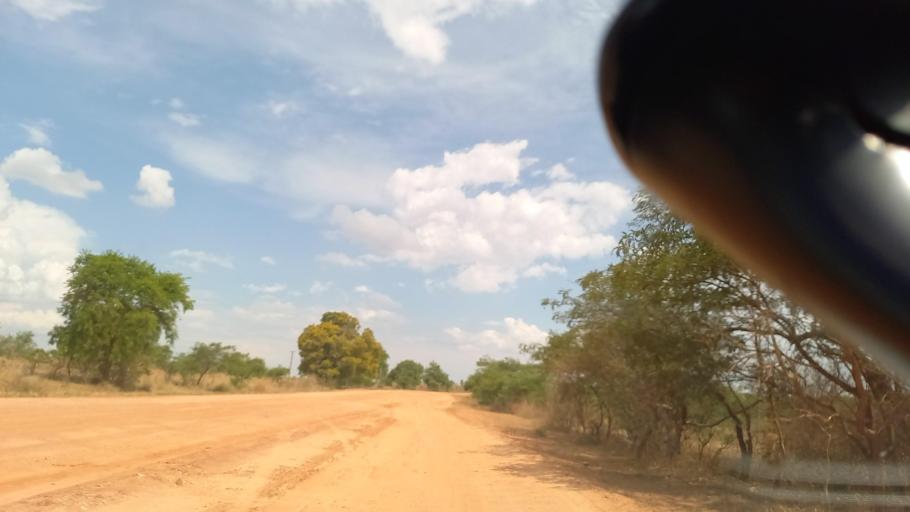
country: ZM
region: Lusaka
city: Kafue
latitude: -16.1215
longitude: 28.0401
